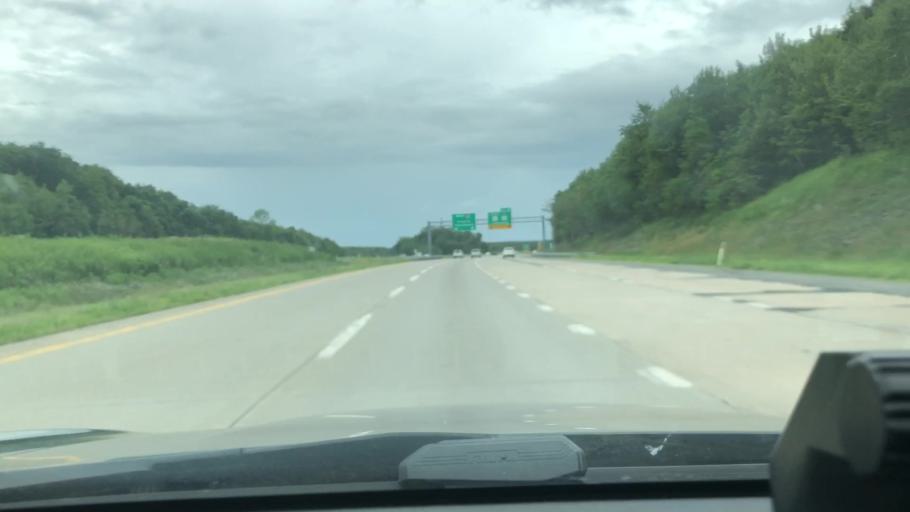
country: US
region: Pennsylvania
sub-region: Monroe County
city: Pocono Pines
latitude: 41.1870
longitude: -75.4385
